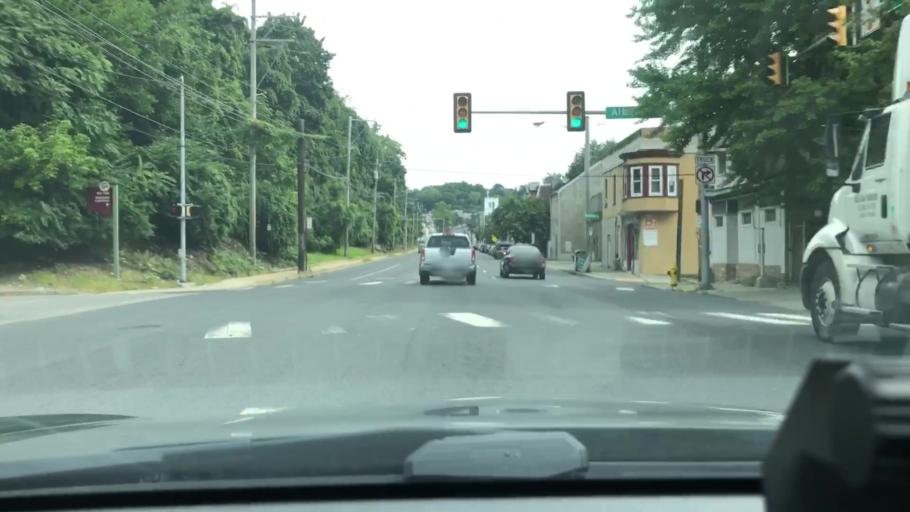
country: US
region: Pennsylvania
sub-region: Lehigh County
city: Fullerton
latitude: 40.6075
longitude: -75.4514
